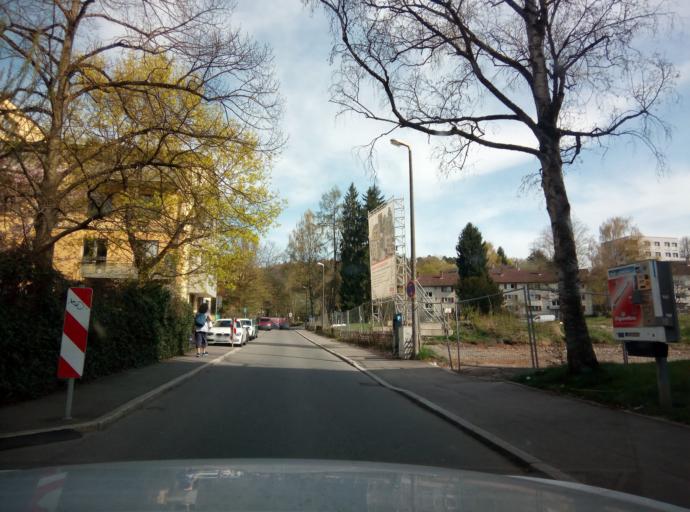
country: DE
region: Baden-Wuerttemberg
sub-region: Tuebingen Region
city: Tuebingen
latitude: 48.5108
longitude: 9.0743
